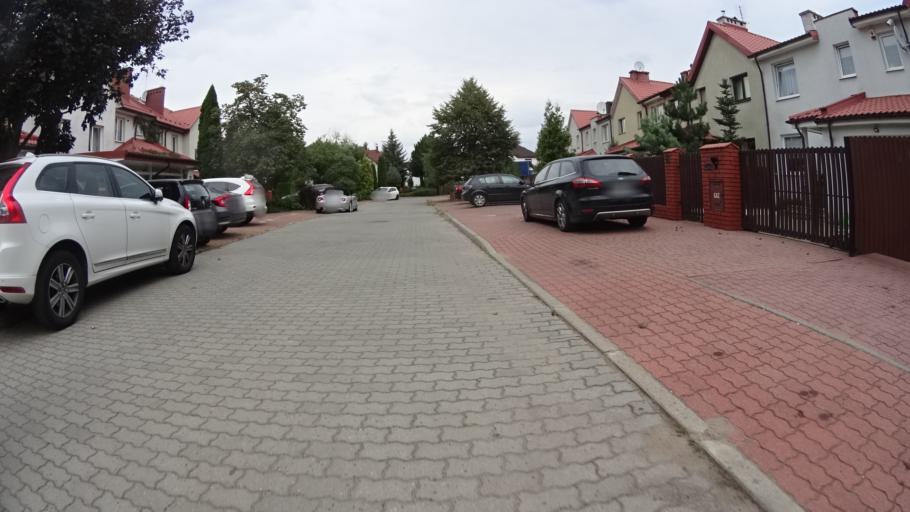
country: PL
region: Masovian Voivodeship
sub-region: Powiat pruszkowski
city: Nadarzyn
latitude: 52.1070
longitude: 20.7973
